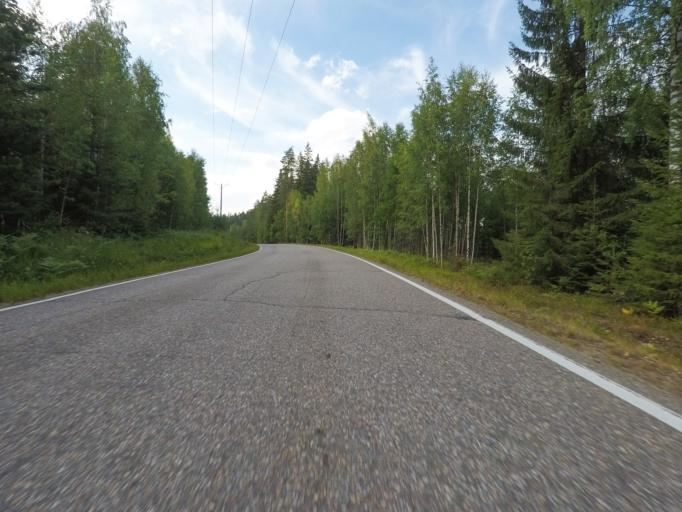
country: FI
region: Southern Savonia
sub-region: Savonlinna
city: Sulkava
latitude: 61.7340
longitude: 28.2089
